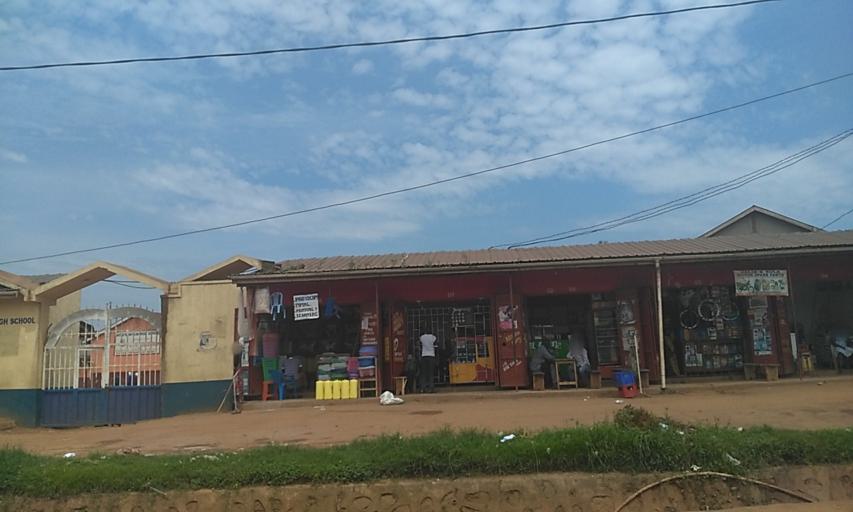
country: UG
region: Central Region
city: Kampala Central Division
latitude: 0.2987
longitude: 32.5308
